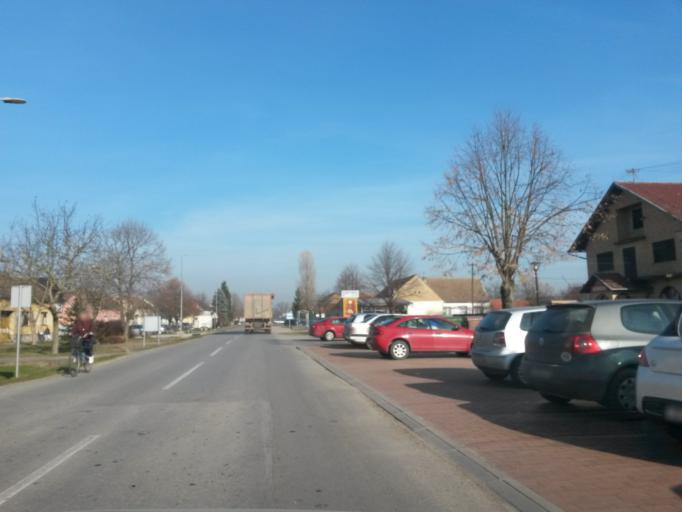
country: HR
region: Vukovarsko-Srijemska
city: Privlaka
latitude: 45.1948
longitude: 18.8384
